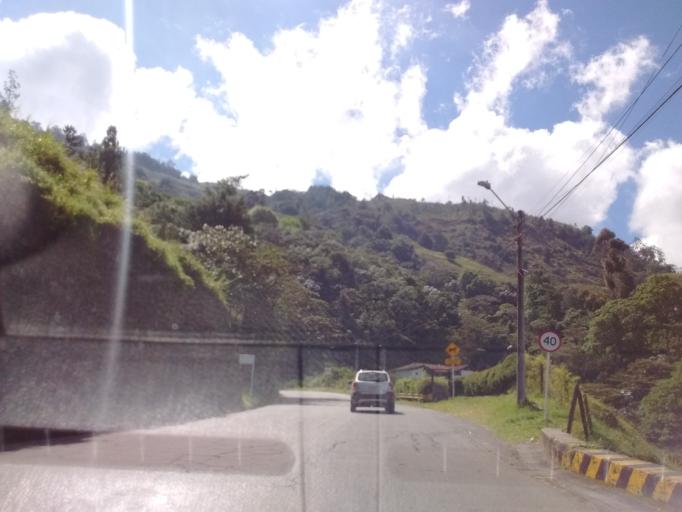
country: CO
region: Antioquia
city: Medellin
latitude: 6.2408
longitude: -75.5157
